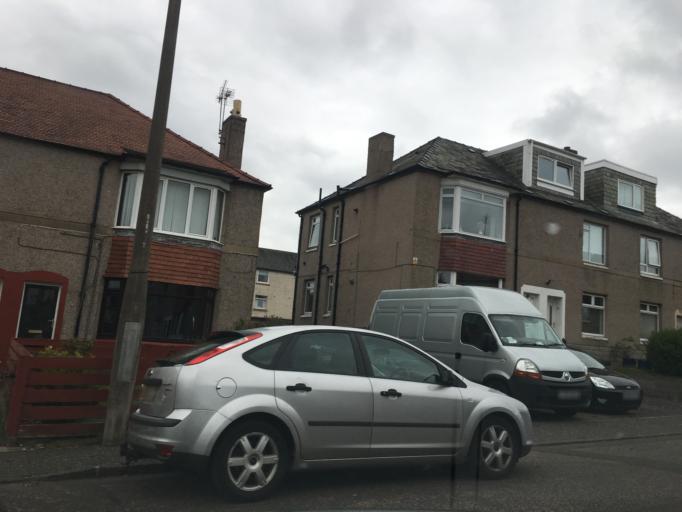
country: GB
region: Scotland
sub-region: Edinburgh
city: Colinton
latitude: 55.9206
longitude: -3.2839
